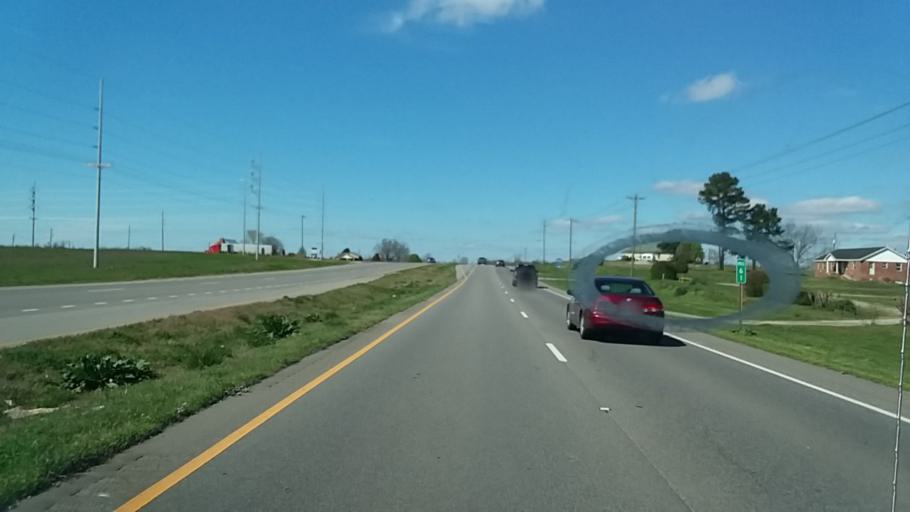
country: US
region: Alabama
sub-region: Morgan County
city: Trinity
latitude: 34.6348
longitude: -87.1108
